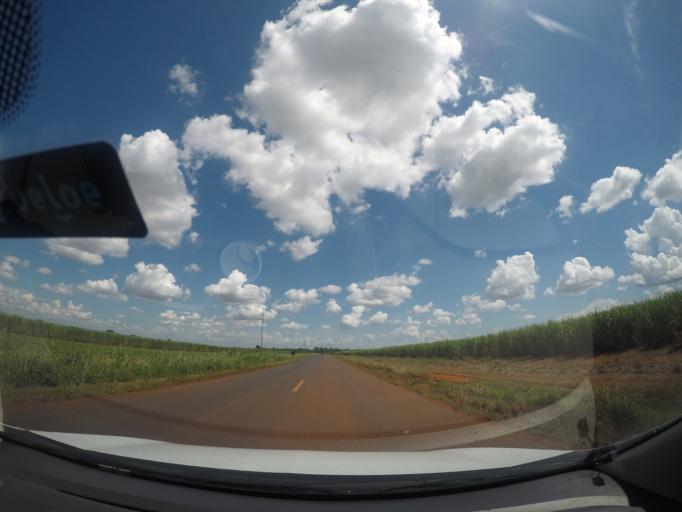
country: BR
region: Minas Gerais
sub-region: Frutal
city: Frutal
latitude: -19.8302
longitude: -48.7341
